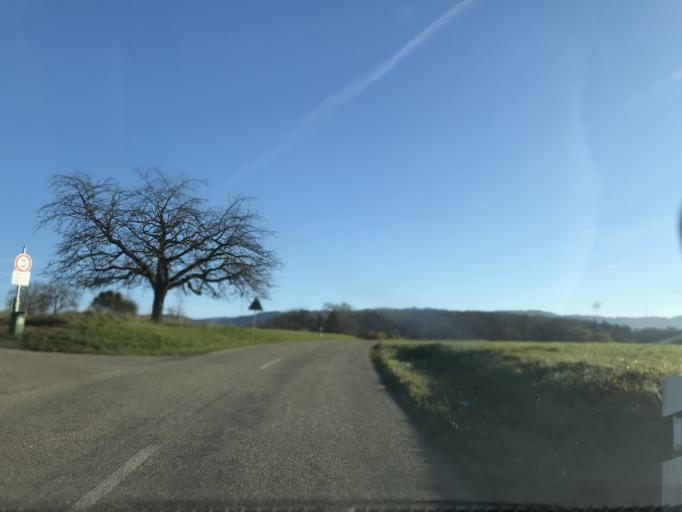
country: DE
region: Baden-Wuerttemberg
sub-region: Freiburg Region
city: Schworstadt
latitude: 47.6158
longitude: 7.8633
